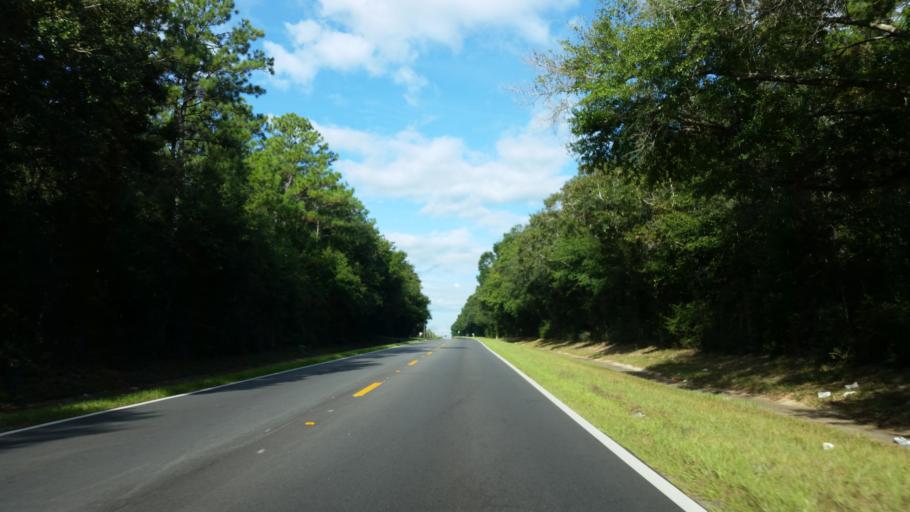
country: US
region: Florida
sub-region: Santa Rosa County
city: Wallace
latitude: 30.6473
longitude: -87.1370
